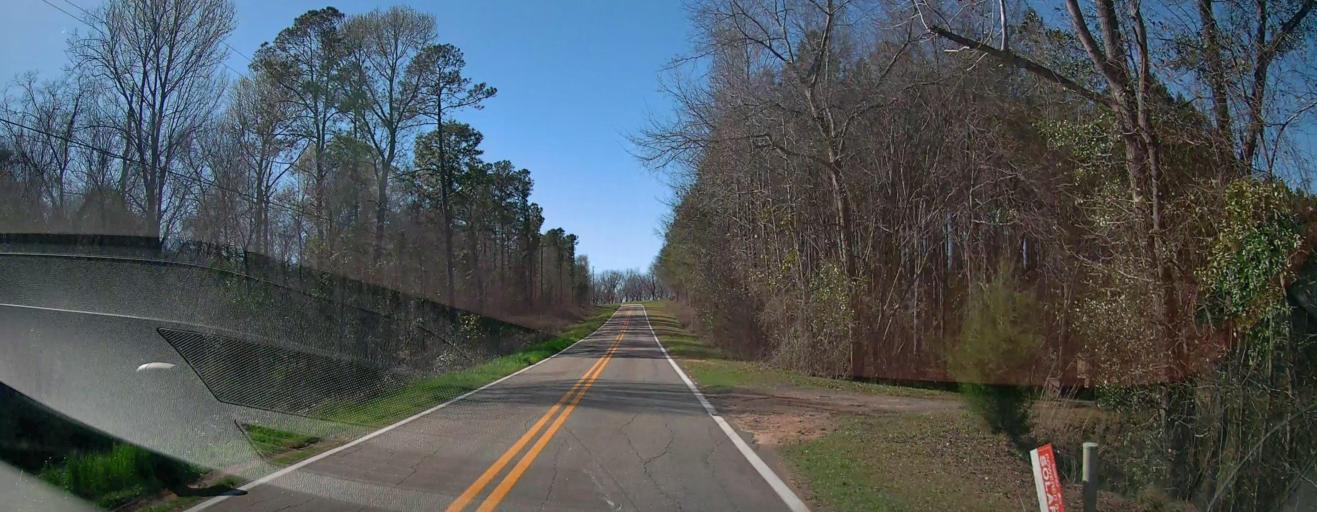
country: US
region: Georgia
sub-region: Peach County
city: Fort Valley
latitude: 32.6120
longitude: -83.8987
